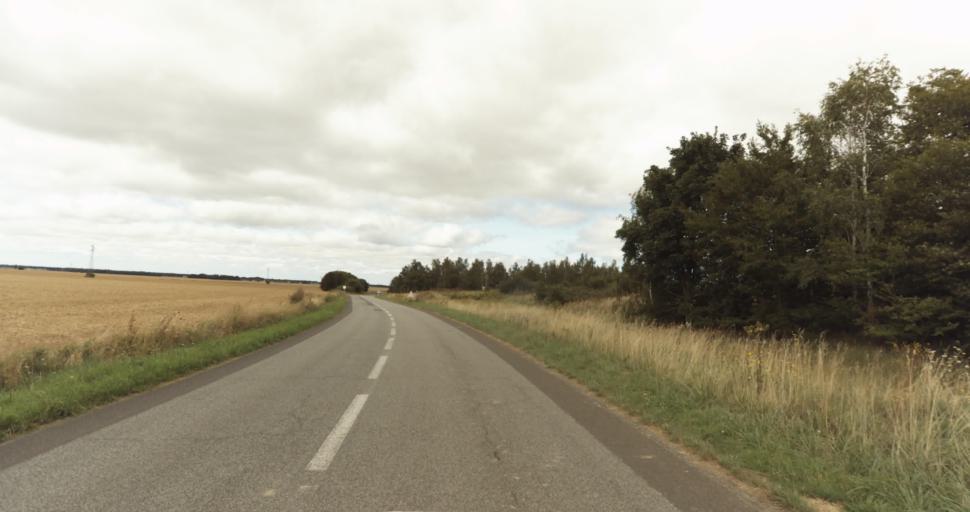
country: FR
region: Haute-Normandie
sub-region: Departement de l'Eure
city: Evreux
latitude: 48.9501
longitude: 1.2027
